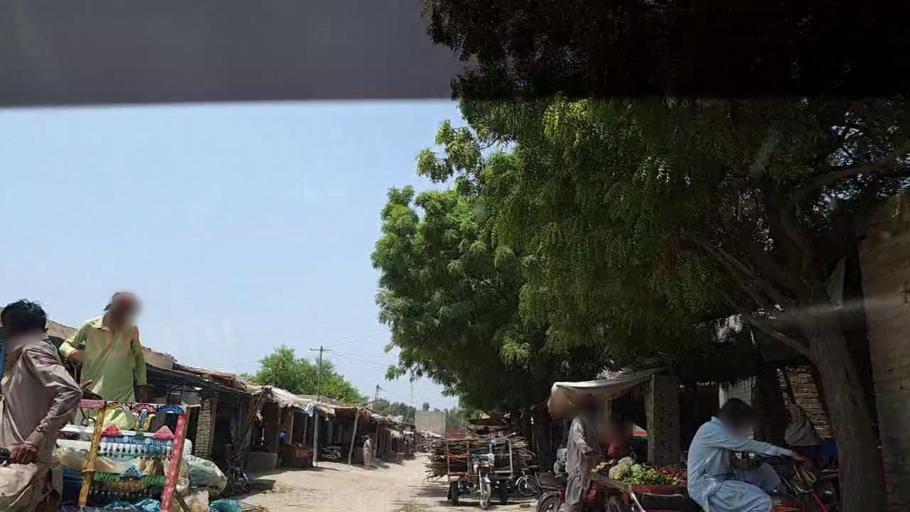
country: PK
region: Sindh
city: Pano Aqil
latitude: 27.9209
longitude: 69.1958
